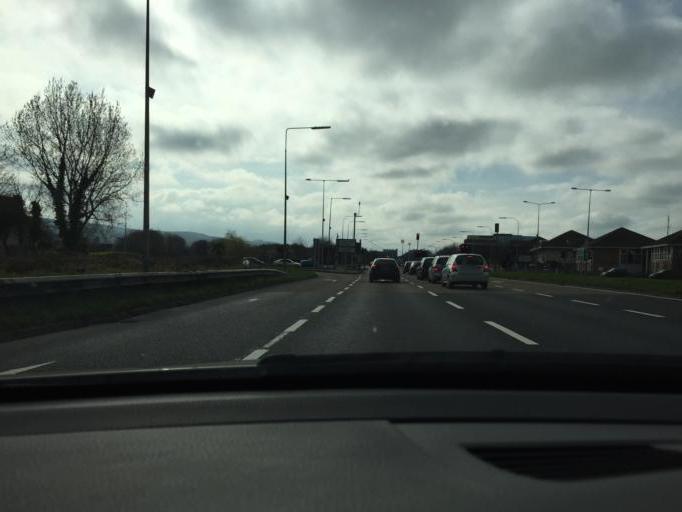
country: IE
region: Leinster
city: Oldbawn
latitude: 53.2863
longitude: -6.3604
